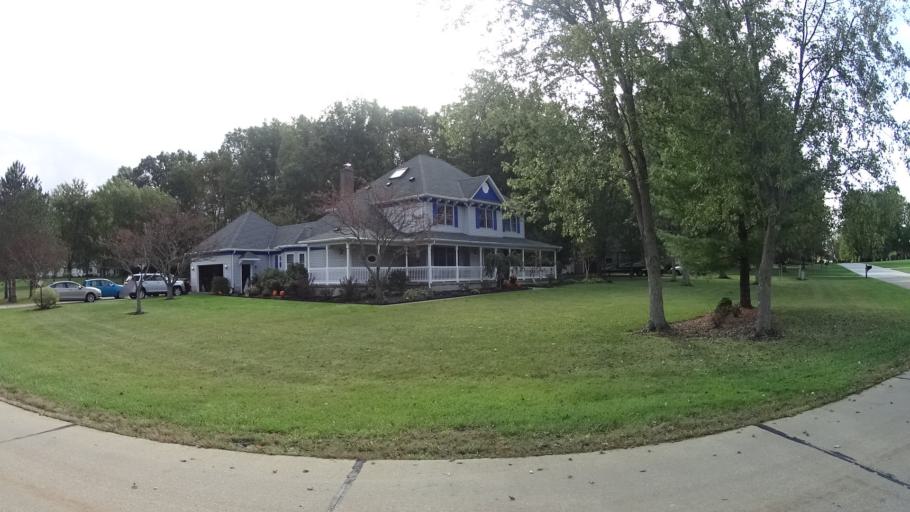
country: US
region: Ohio
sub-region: Lorain County
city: Grafton
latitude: 41.3284
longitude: -82.0651
